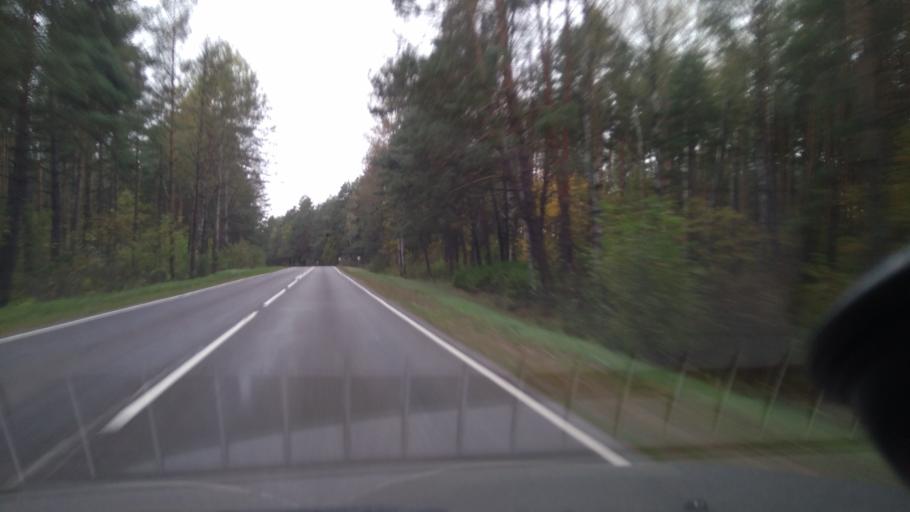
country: BY
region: Minsk
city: Svislach
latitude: 53.6395
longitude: 27.9037
